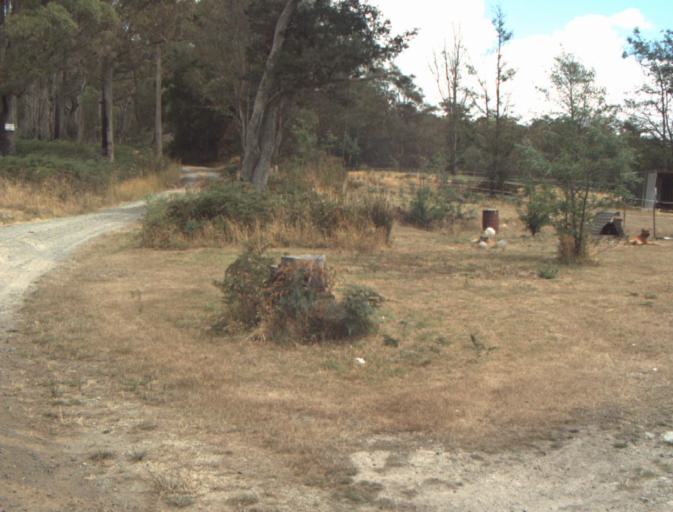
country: AU
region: Tasmania
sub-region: Launceston
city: Mayfield
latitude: -41.1987
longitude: 147.1683
